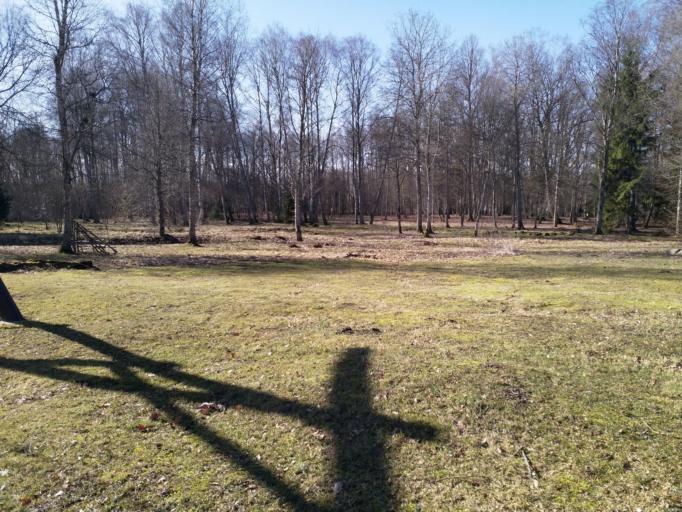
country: LV
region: Aizpute
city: Aizpute
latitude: 56.8323
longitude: 21.7753
